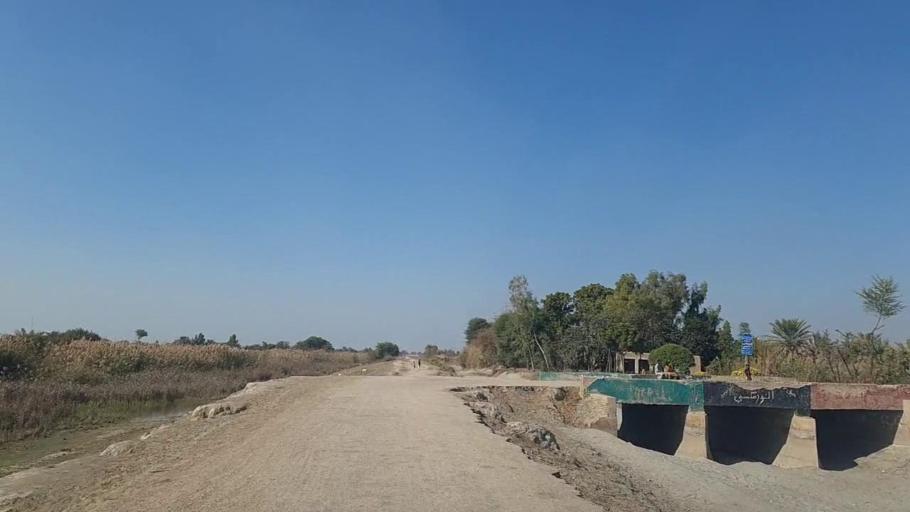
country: PK
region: Sindh
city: Jam Sahib
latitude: 26.2224
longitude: 68.6017
